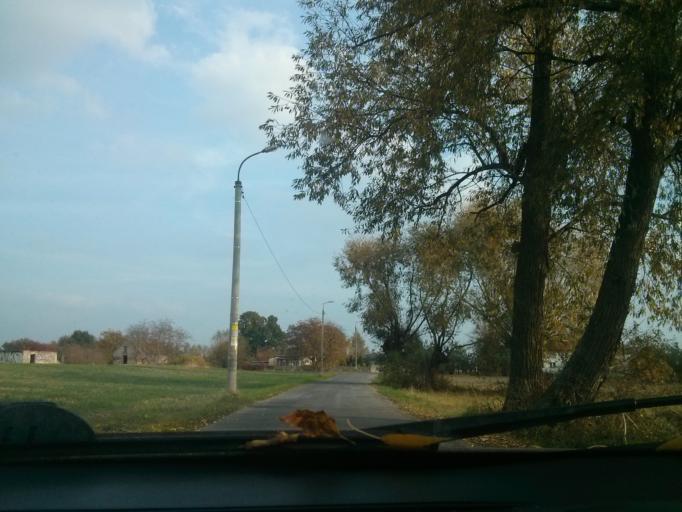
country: PL
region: Masovian Voivodeship
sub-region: Powiat piaseczynski
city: Konstancin-Jeziorna
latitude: 52.1378
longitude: 21.1480
